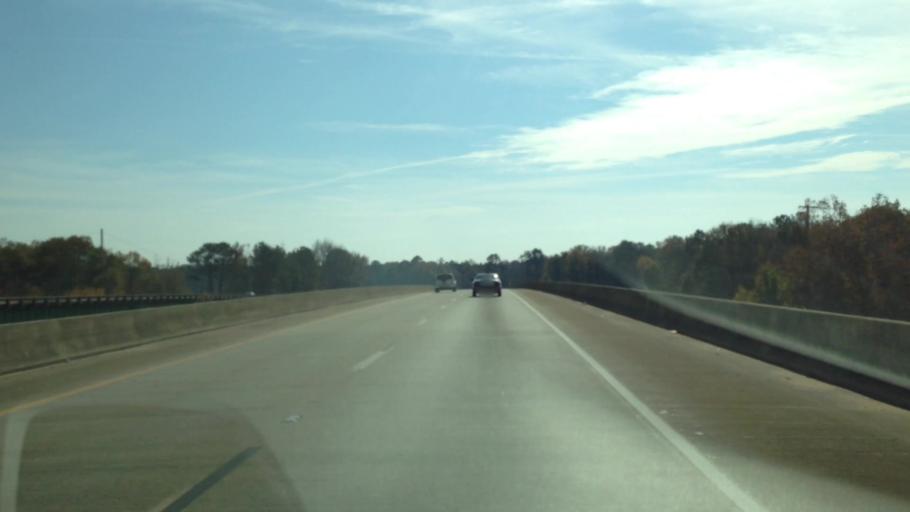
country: US
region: Alabama
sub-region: Autauga County
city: Prattville
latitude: 32.4114
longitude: -86.4085
